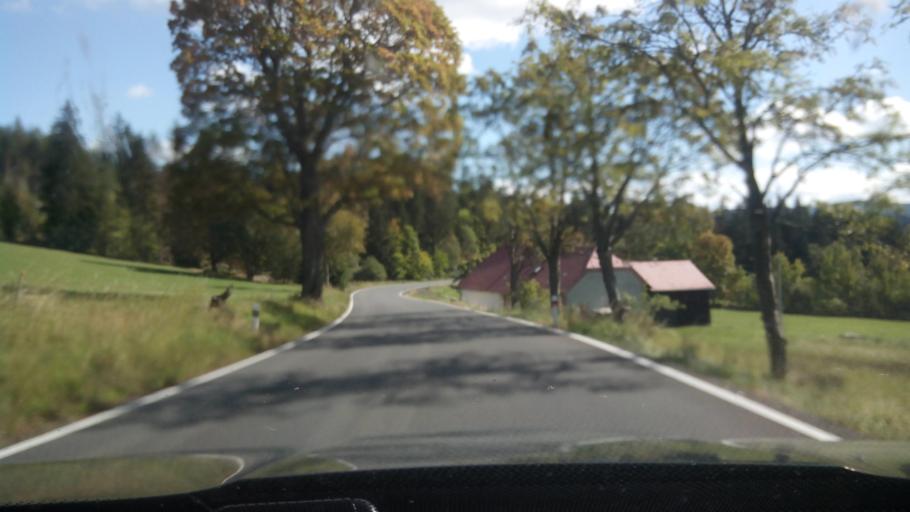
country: CZ
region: Jihocesky
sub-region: Okres Prachatice
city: Stachy
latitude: 49.1108
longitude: 13.6527
